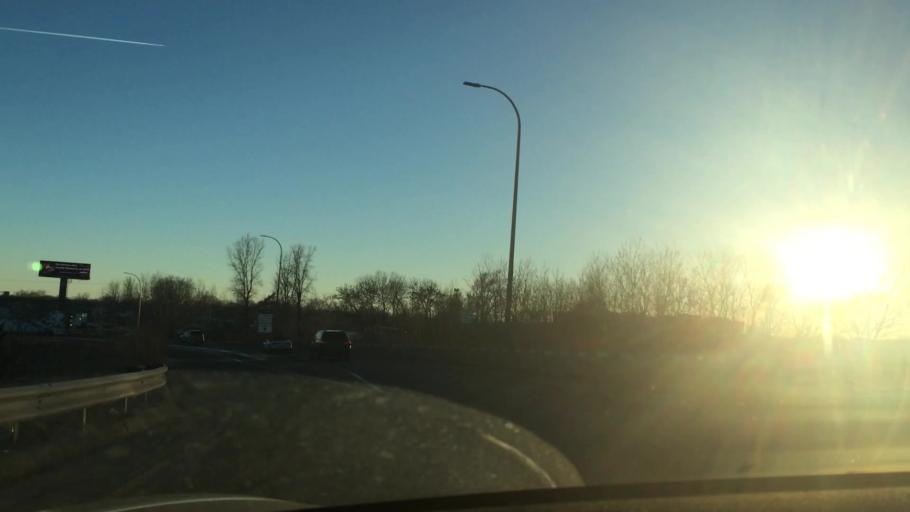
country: US
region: Minnesota
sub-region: Ramsey County
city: Mounds View
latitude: 45.1275
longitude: -93.1893
